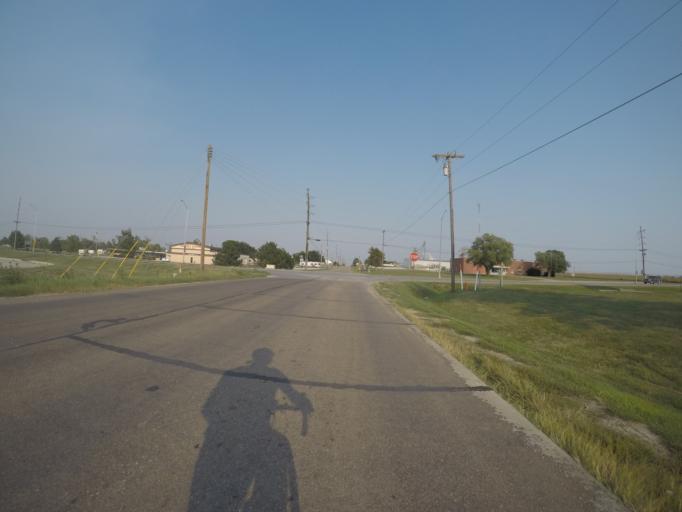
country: US
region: Nebraska
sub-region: Gage County
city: Beatrice
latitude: 40.2629
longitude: -96.7852
